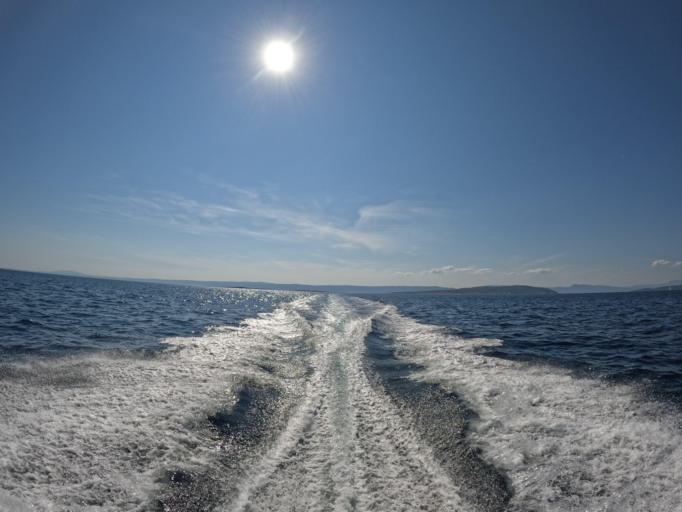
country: HR
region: Primorsko-Goranska
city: Punat
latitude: 44.9550
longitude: 14.6010
